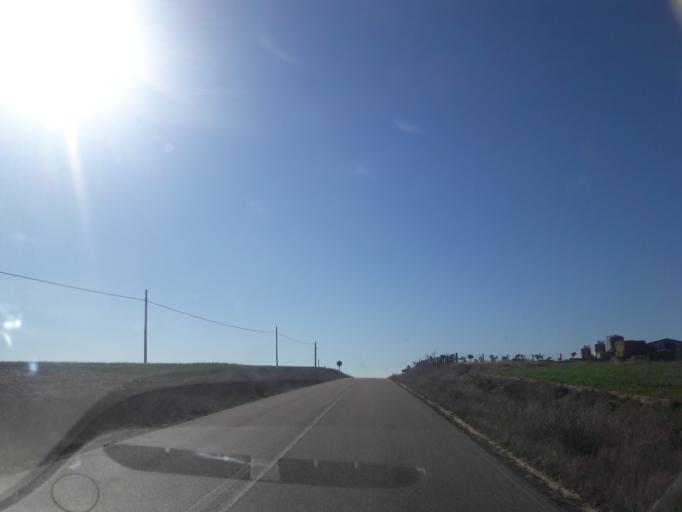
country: ES
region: Castille and Leon
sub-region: Provincia de Salamanca
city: Macotera
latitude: 40.8415
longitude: -5.3073
